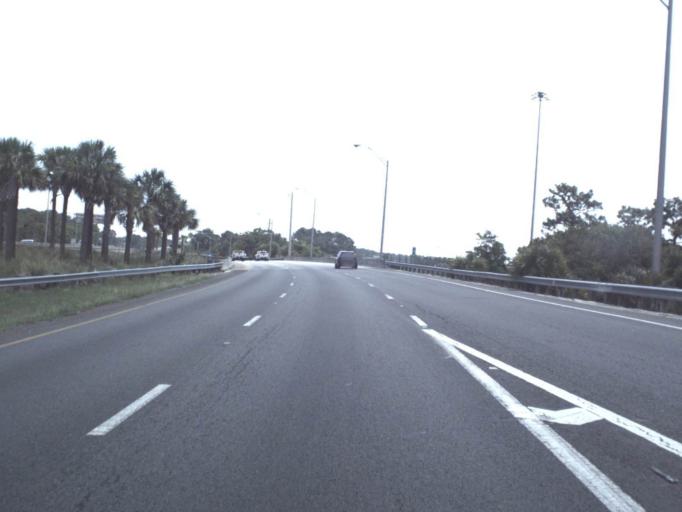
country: US
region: Florida
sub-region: Duval County
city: Jacksonville
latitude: 30.3496
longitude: -81.5534
